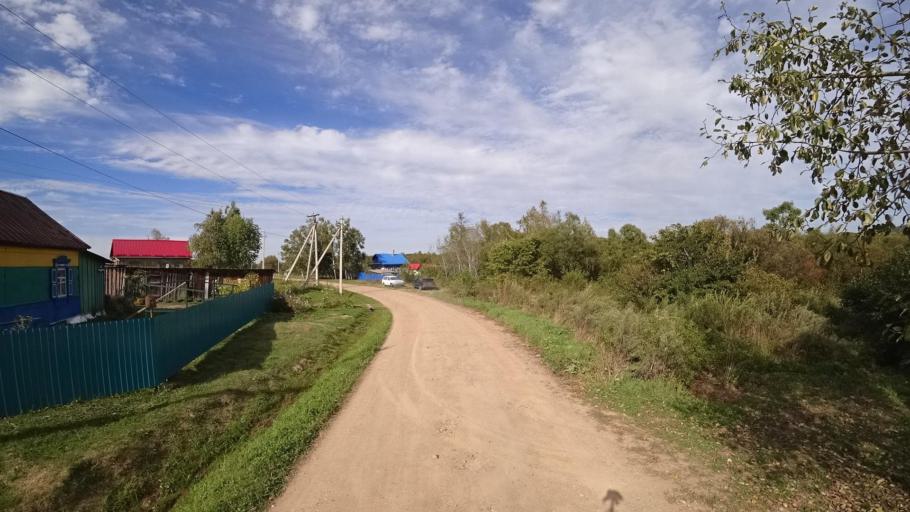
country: RU
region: Primorskiy
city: Dostoyevka
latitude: 44.2985
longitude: 133.4639
